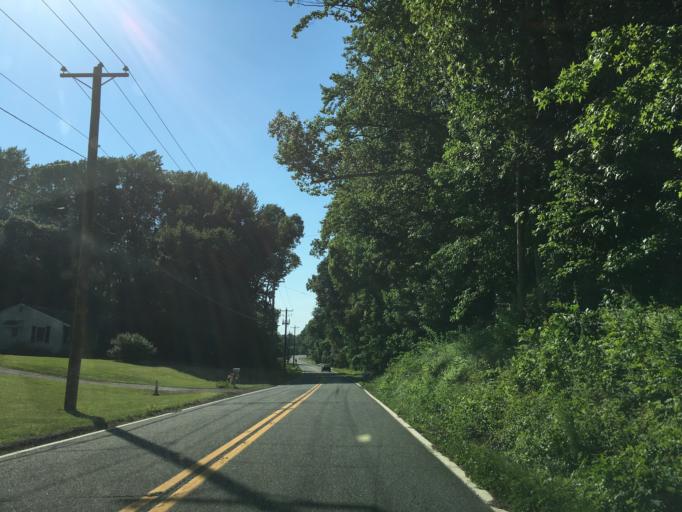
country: US
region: Maryland
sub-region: Queen Anne's County
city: Grasonville
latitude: 38.9834
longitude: -76.1446
